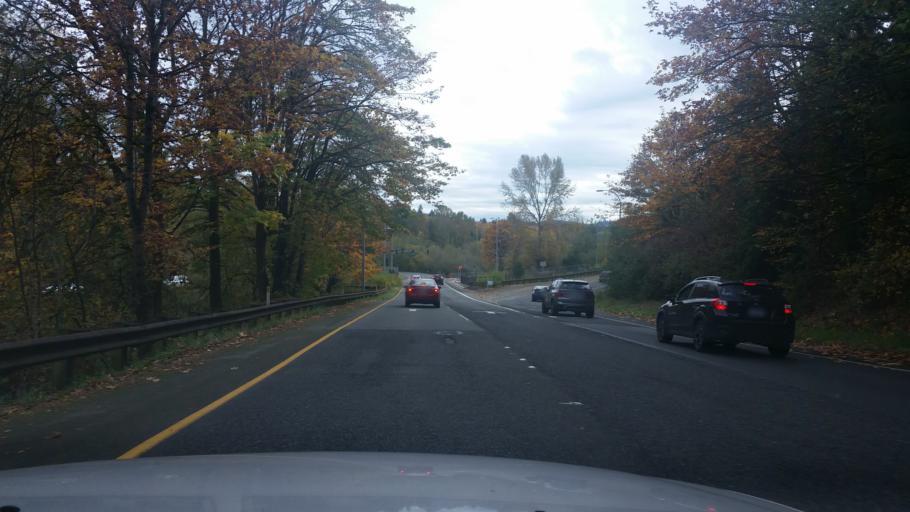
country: US
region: Washington
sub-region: King County
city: Newport
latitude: 47.5993
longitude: -122.1689
